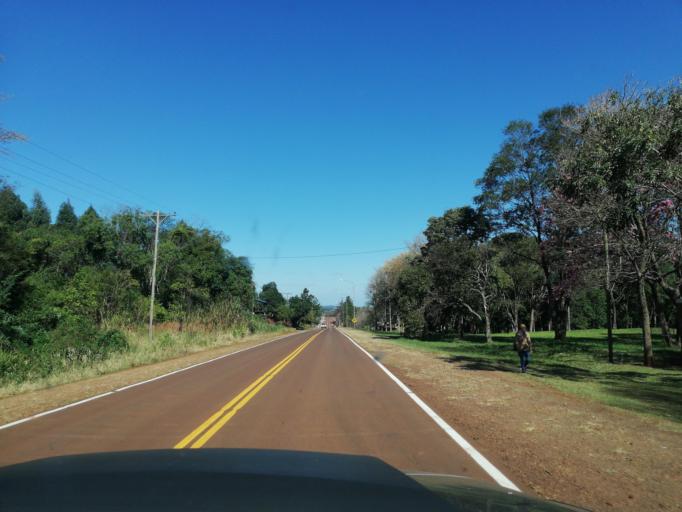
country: AR
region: Misiones
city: Aristobulo del Valle
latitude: -27.0768
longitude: -54.8319
